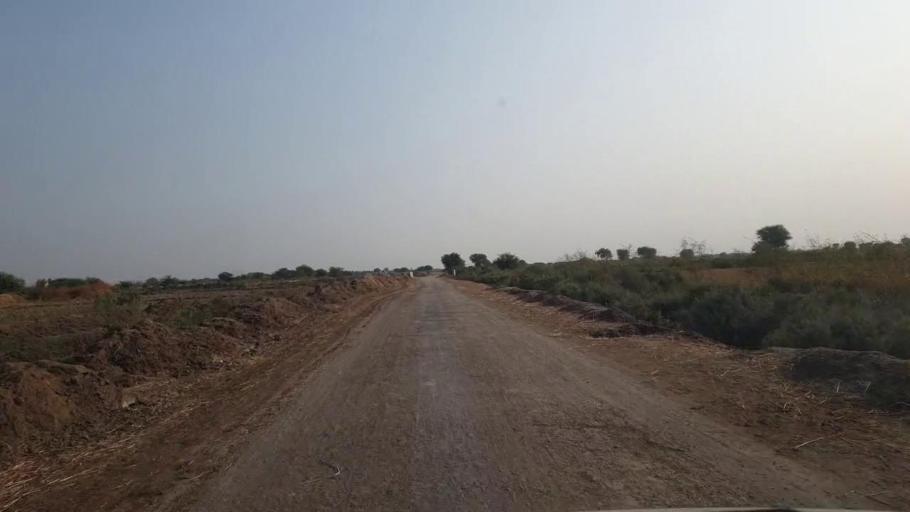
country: PK
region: Sindh
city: Matli
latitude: 25.0570
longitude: 68.7625
